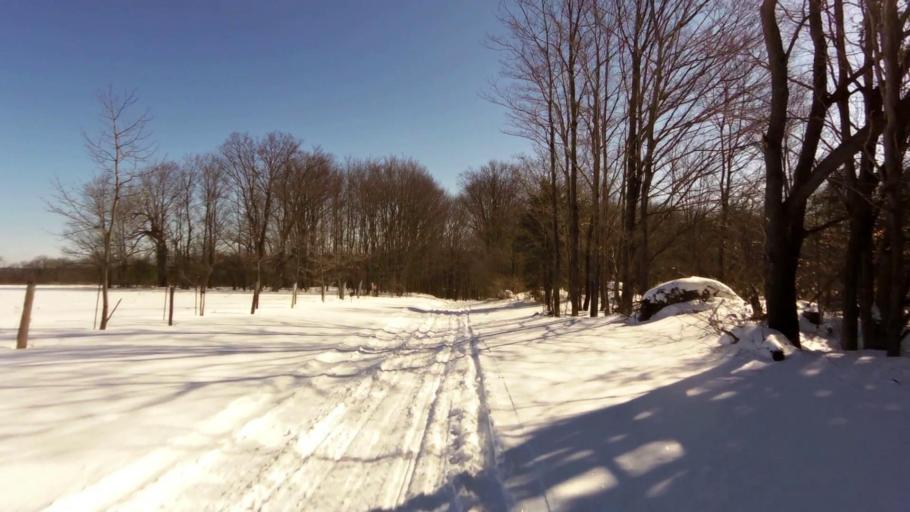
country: US
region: New York
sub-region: Cattaraugus County
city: Franklinville
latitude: 42.3435
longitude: -78.3539
